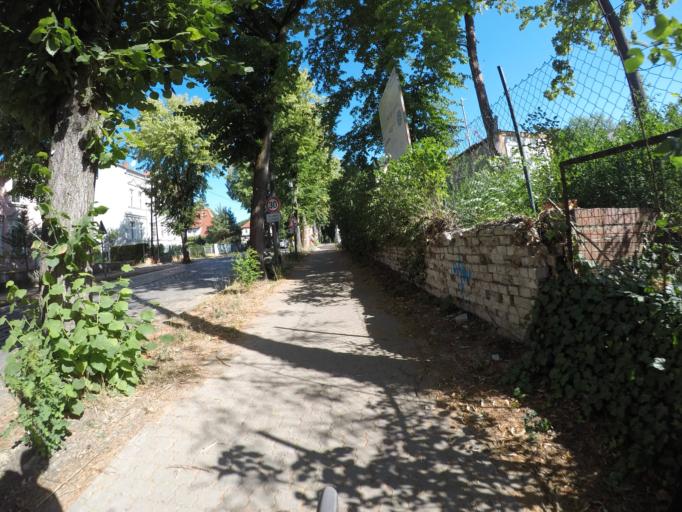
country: DE
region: Brandenburg
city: Woltersdorf
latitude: 52.4454
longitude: 13.7625
